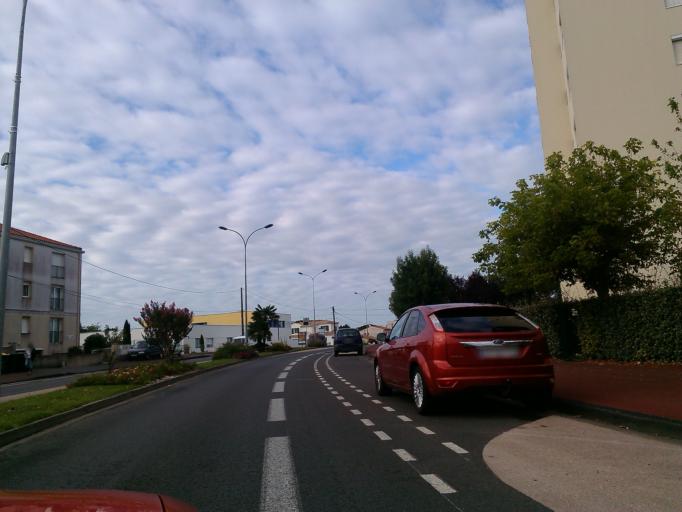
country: FR
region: Poitou-Charentes
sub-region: Departement de la Charente-Maritime
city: Royan
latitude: 45.6341
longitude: -1.0293
